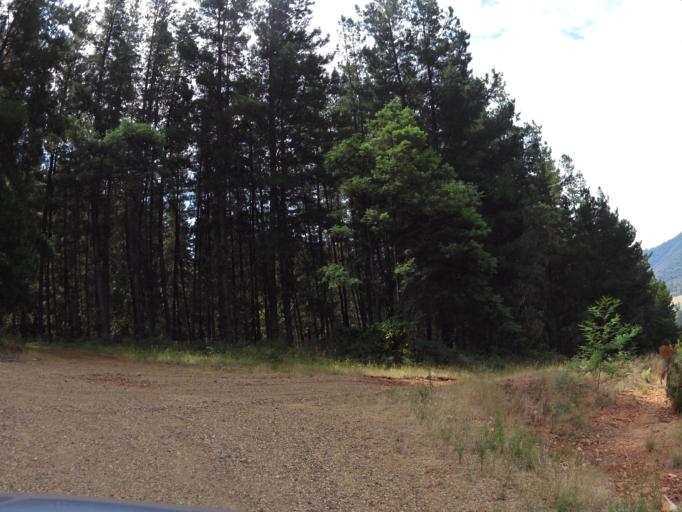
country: AU
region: Victoria
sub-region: Alpine
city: Mount Beauty
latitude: -36.7658
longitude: 147.0176
